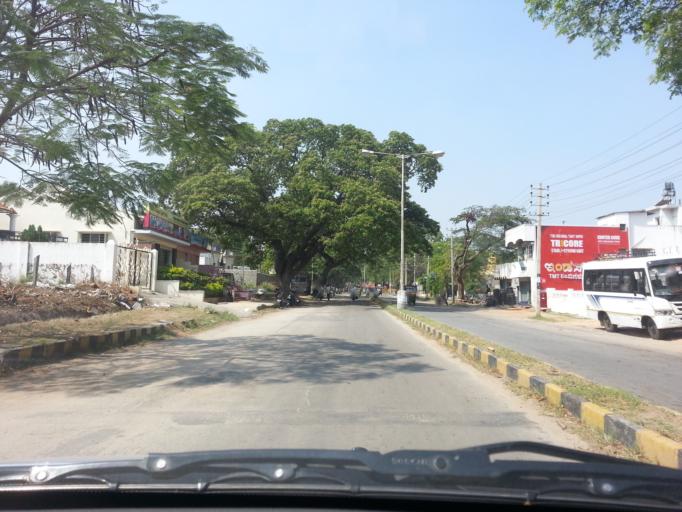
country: IN
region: Karnataka
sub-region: Mysore
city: Mysore
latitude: 12.3267
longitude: 76.6609
